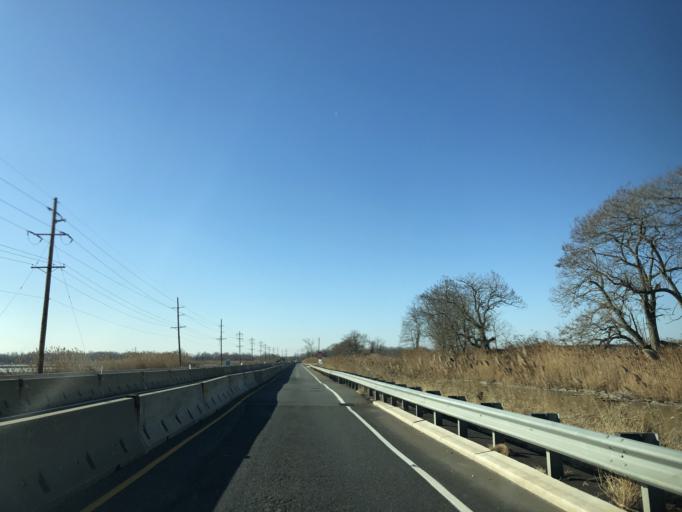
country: US
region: New Jersey
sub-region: Gloucester County
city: Beckett
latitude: 39.7985
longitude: -75.3612
